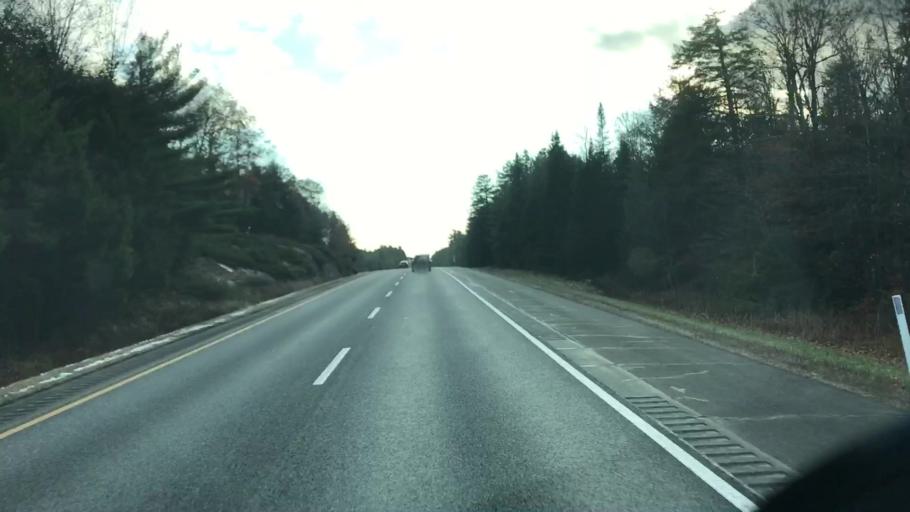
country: US
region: Maine
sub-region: Kennebec County
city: Sidney
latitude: 44.3961
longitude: -69.7560
